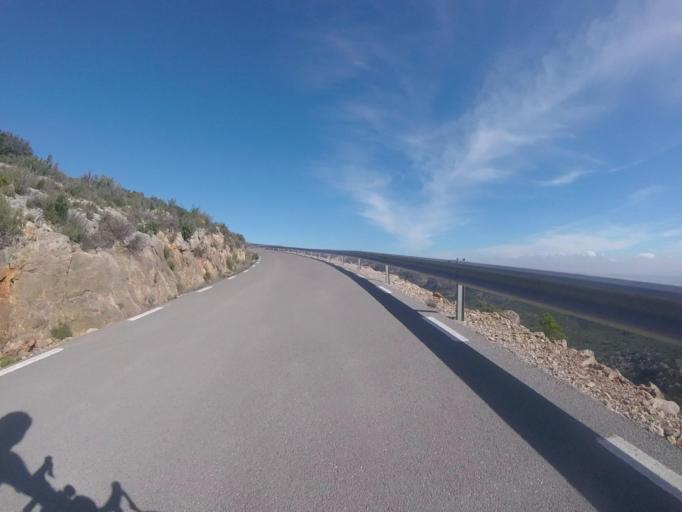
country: ES
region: Valencia
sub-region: Provincia de Castello
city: Sarratella
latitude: 40.2867
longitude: 0.0406
